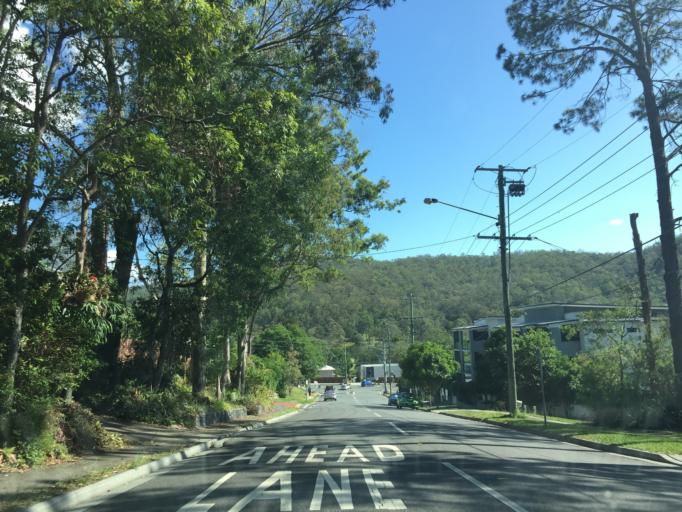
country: AU
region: Queensland
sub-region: Brisbane
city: Taringa
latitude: -27.4478
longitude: 152.9582
